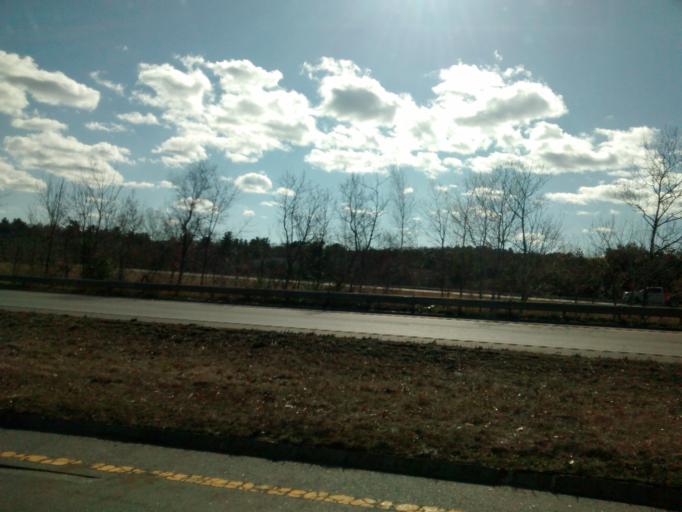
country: US
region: Massachusetts
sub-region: Worcester County
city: East Douglas
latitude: 42.1043
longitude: -71.7046
